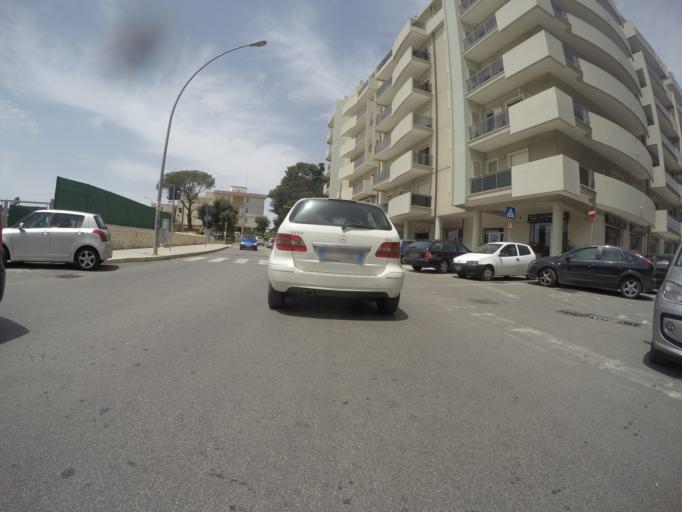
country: IT
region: Apulia
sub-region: Provincia di Taranto
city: Martina Franca
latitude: 40.6978
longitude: 17.3382
